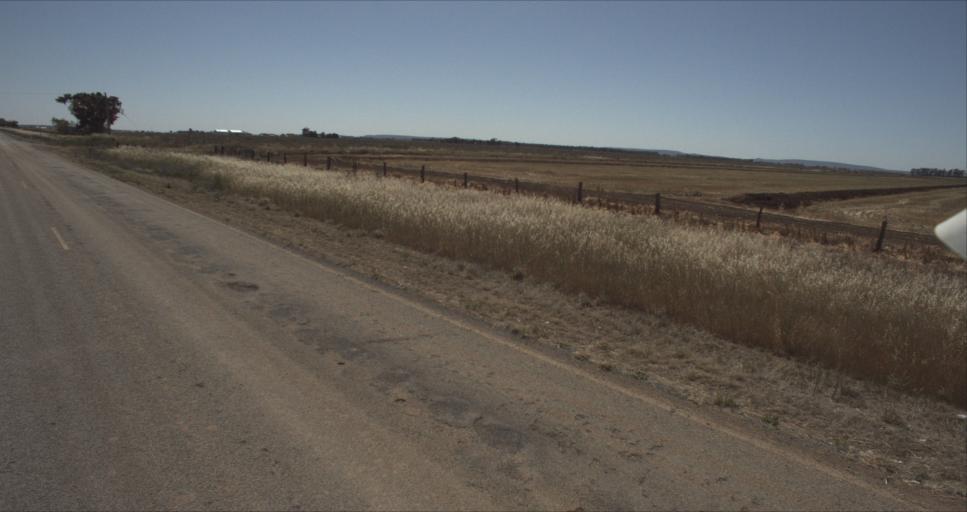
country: AU
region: New South Wales
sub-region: Leeton
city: Leeton
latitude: -34.5149
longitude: 146.2844
